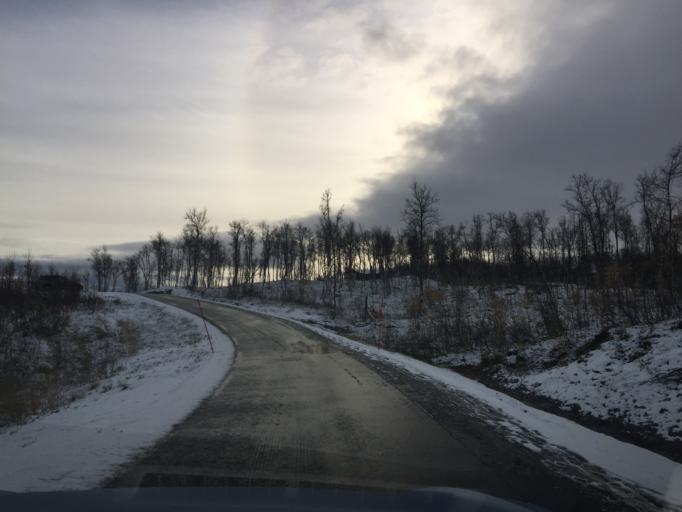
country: NO
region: Nordland
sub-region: Sorfold
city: Straumen
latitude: 67.0877
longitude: 16.0207
